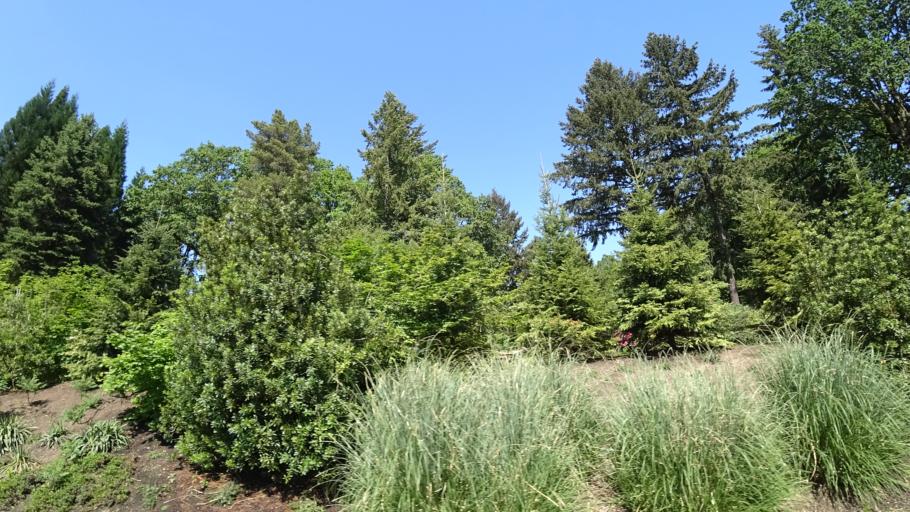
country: US
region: Oregon
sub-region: Washington County
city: Cedar Hills
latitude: 45.5019
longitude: -122.7990
